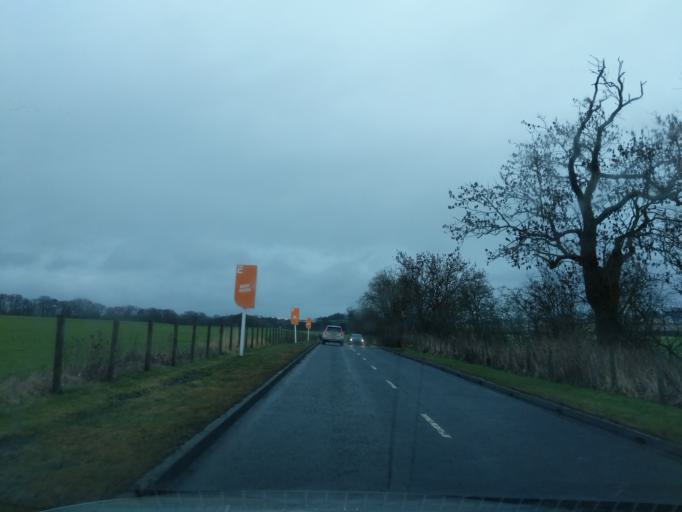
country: GB
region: Scotland
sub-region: Edinburgh
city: Newbridge
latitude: 55.9195
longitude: -3.4090
